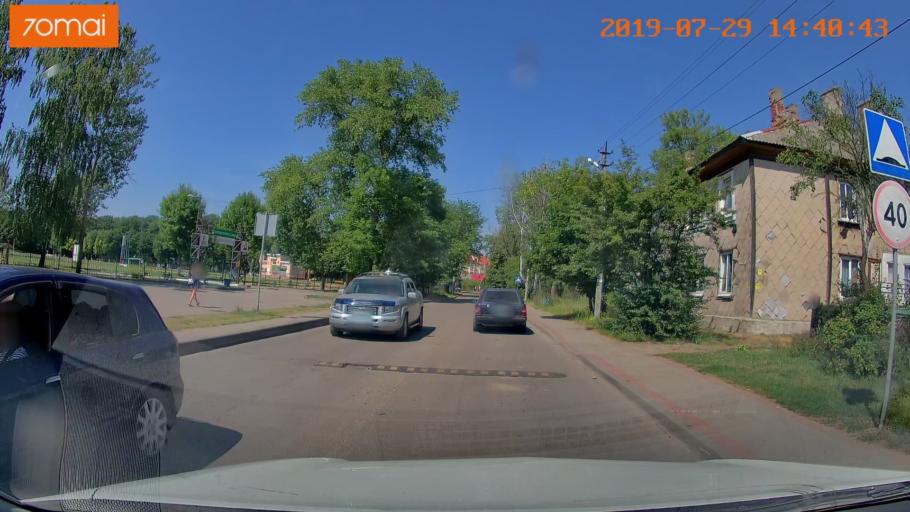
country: RU
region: Kaliningrad
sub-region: Gorod Kaliningrad
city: Baltiysk
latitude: 54.6557
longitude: 19.9007
